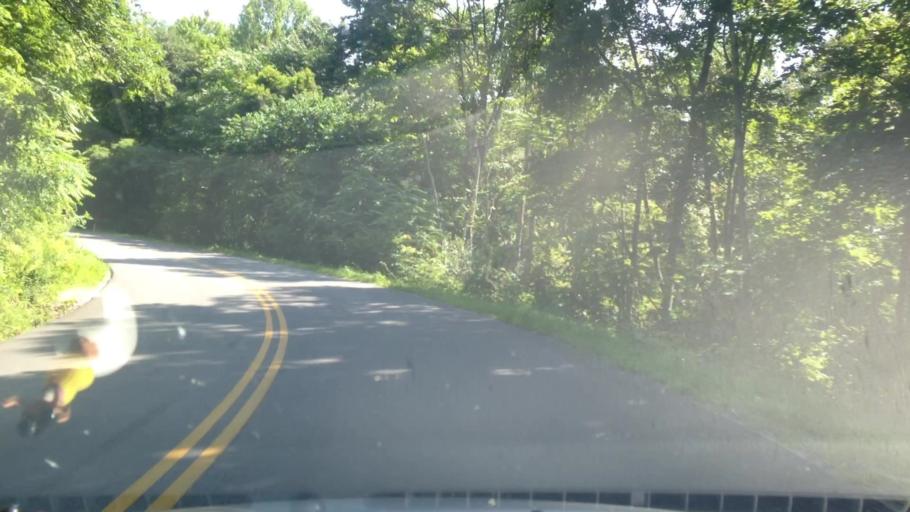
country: US
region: Virginia
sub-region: Patrick County
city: Patrick Springs
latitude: 36.5995
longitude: -80.1697
